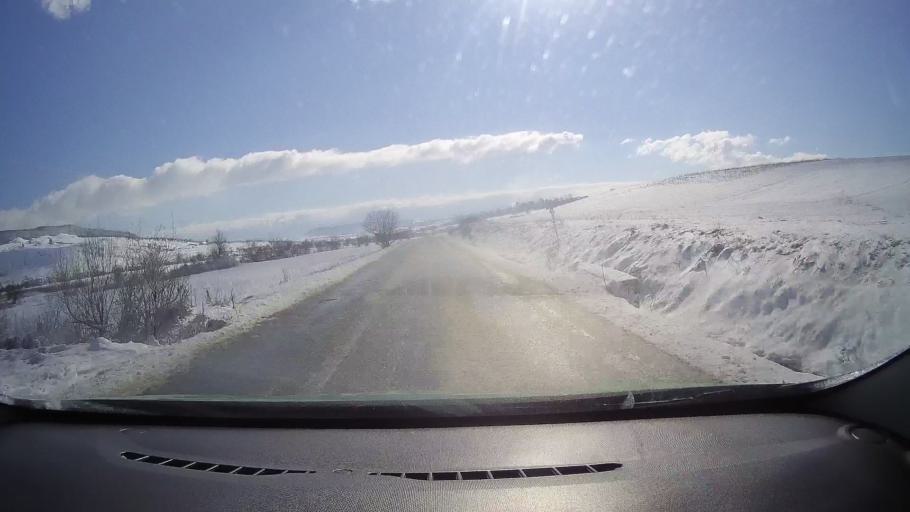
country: RO
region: Sibiu
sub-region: Comuna Rosia
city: Rosia
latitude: 45.8280
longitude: 24.3133
